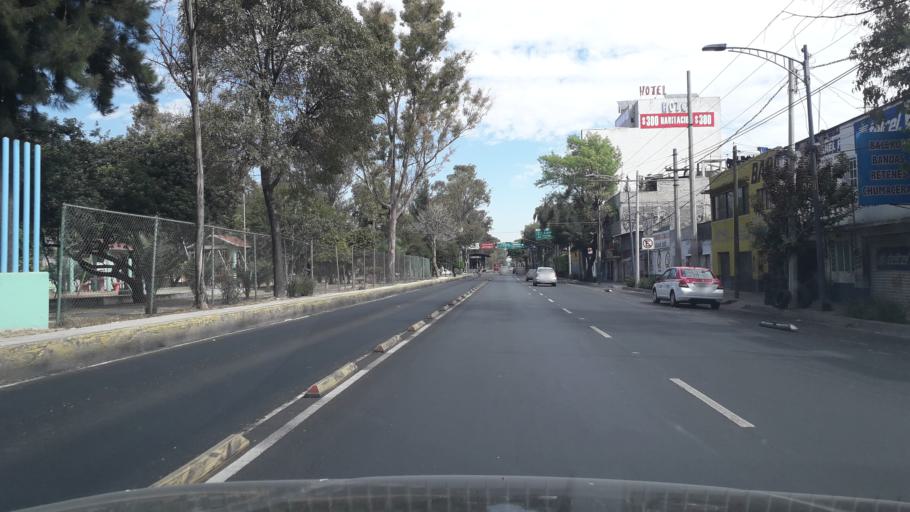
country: MX
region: Mexico City
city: Gustavo A. Madero
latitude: 19.4691
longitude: -99.1019
